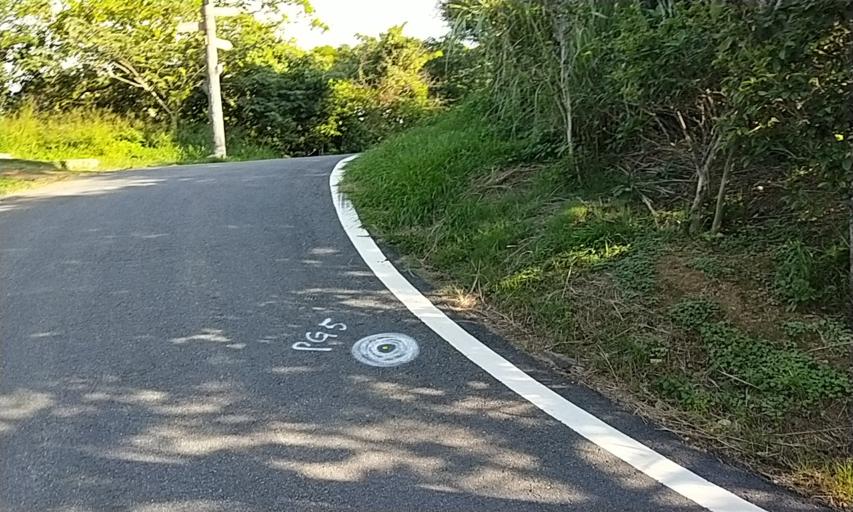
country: TW
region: Taiwan
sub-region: Hsinchu
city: Hsinchu
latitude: 24.7711
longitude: 120.9294
